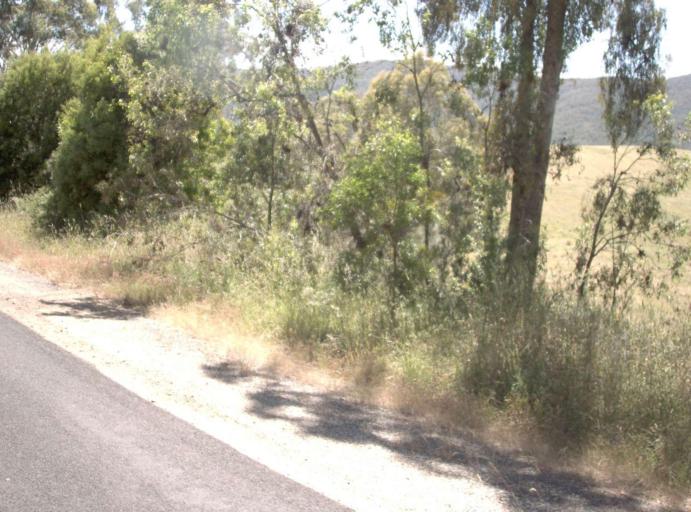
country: AU
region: Victoria
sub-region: East Gippsland
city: Lakes Entrance
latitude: -37.4225
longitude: 148.2026
